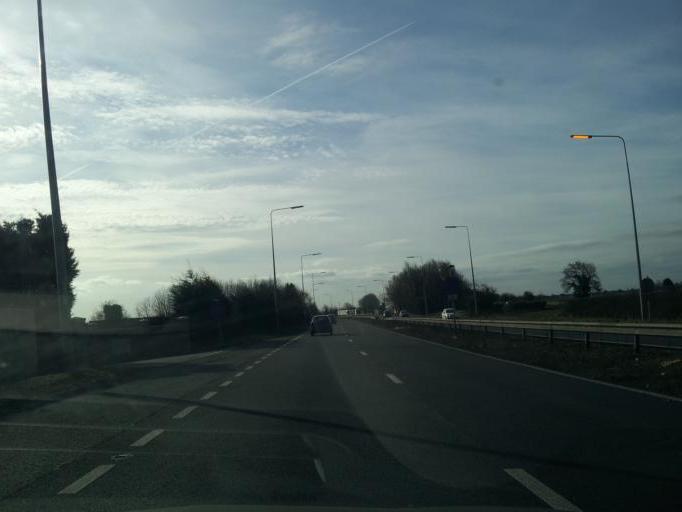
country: GB
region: England
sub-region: Central Bedfordshire
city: Sandy
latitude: 52.1122
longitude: -0.2832
